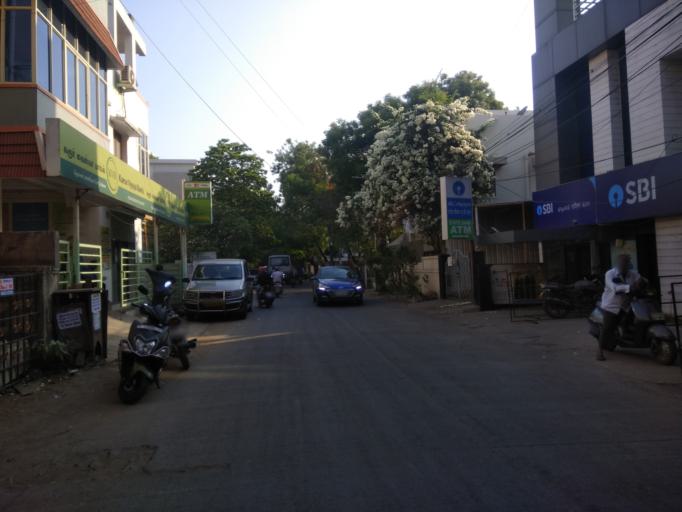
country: IN
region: Tamil Nadu
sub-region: Chennai
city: Chetput
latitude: 13.0695
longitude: 80.2243
